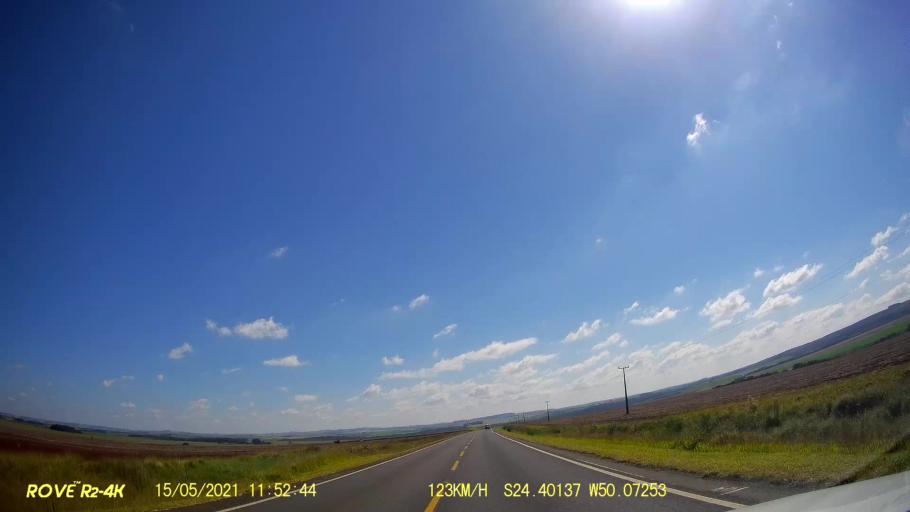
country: BR
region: Parana
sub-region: Pirai Do Sul
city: Pirai do Sul
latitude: -24.4017
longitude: -50.0727
